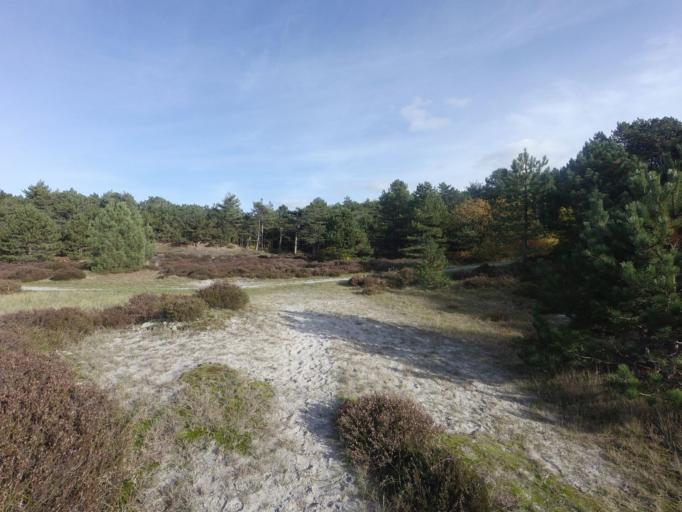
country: NL
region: North Holland
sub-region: Gemeente Bergen
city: Egmond aan Zee
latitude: 52.7130
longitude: 4.6553
